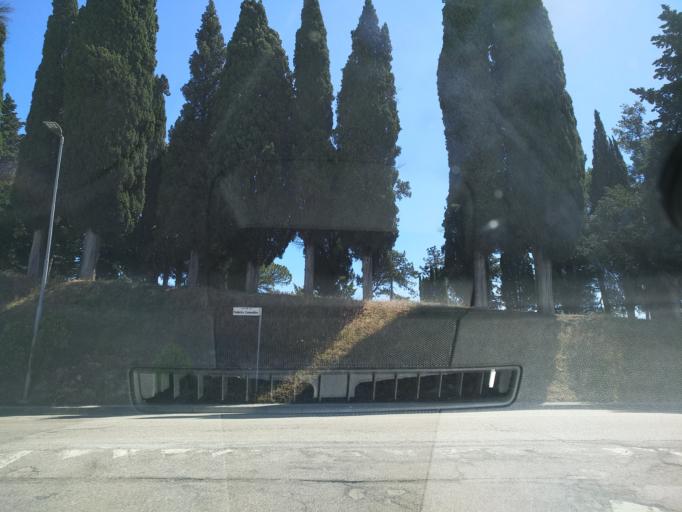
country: IT
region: The Marches
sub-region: Provincia di Pesaro e Urbino
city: Urbino
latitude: 43.7321
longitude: 12.6318
